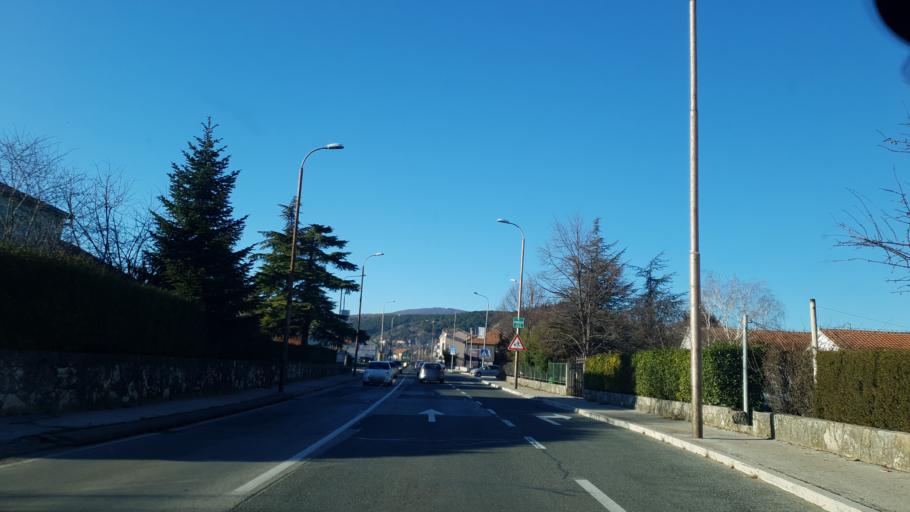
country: HR
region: Splitsko-Dalmatinska
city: Sinj
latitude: 43.6941
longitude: 16.6416
